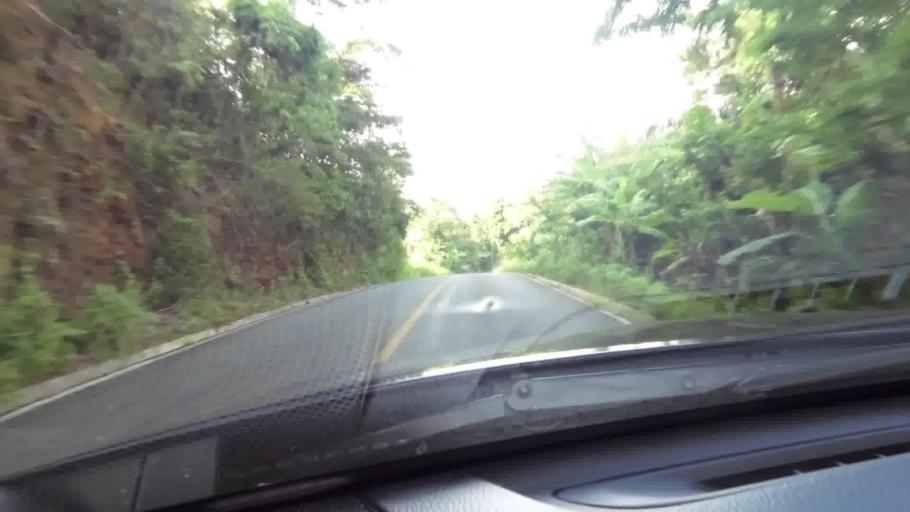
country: BR
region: Espirito Santo
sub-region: Guarapari
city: Guarapari
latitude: -20.5921
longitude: -40.5390
